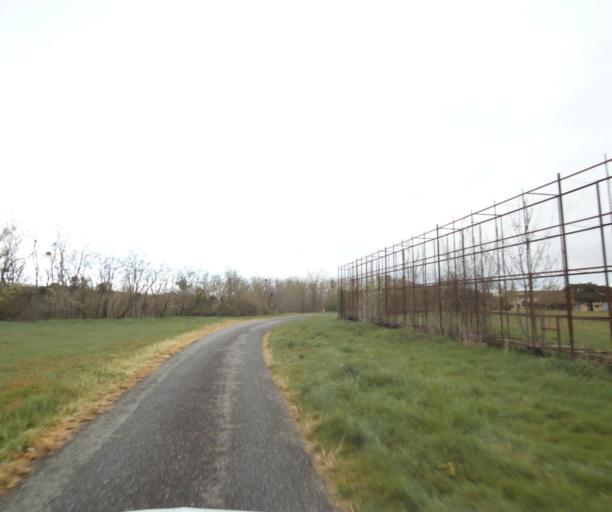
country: FR
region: Midi-Pyrenees
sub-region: Departement de l'Ariege
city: Saverdun
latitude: 43.2150
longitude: 1.5998
